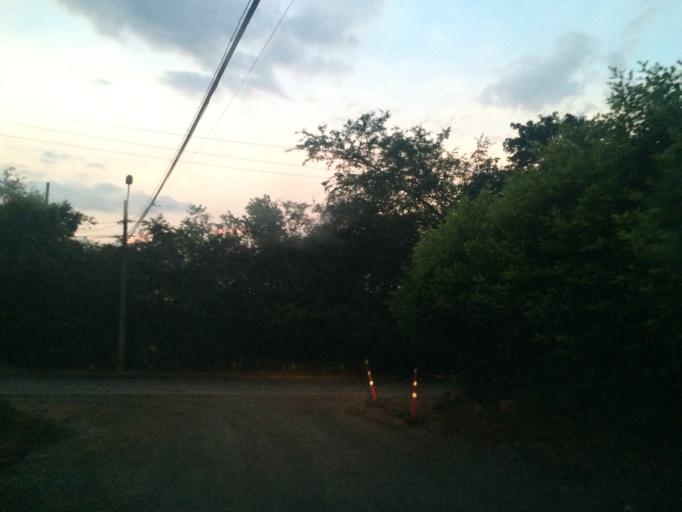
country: CO
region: Valle del Cauca
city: Jamundi
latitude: 3.3470
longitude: -76.5271
